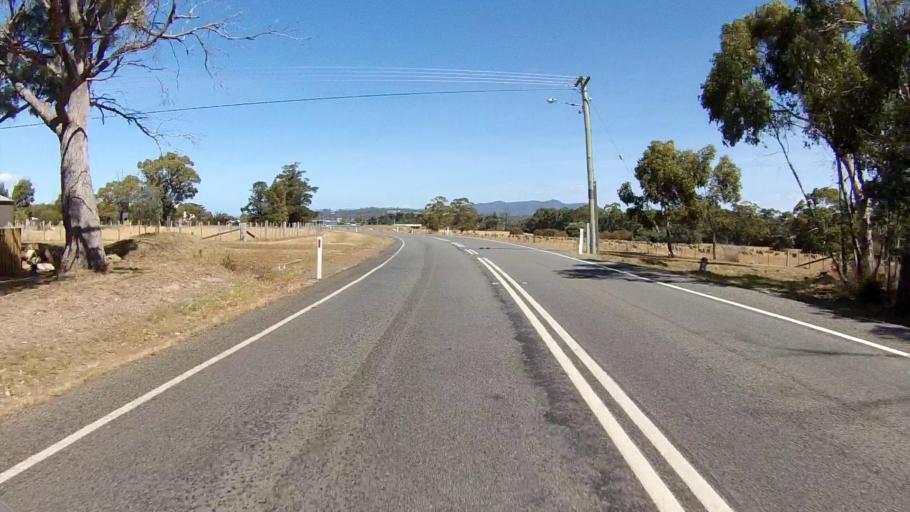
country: AU
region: Tasmania
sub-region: Sorell
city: Sorell
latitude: -42.5044
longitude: 147.9083
